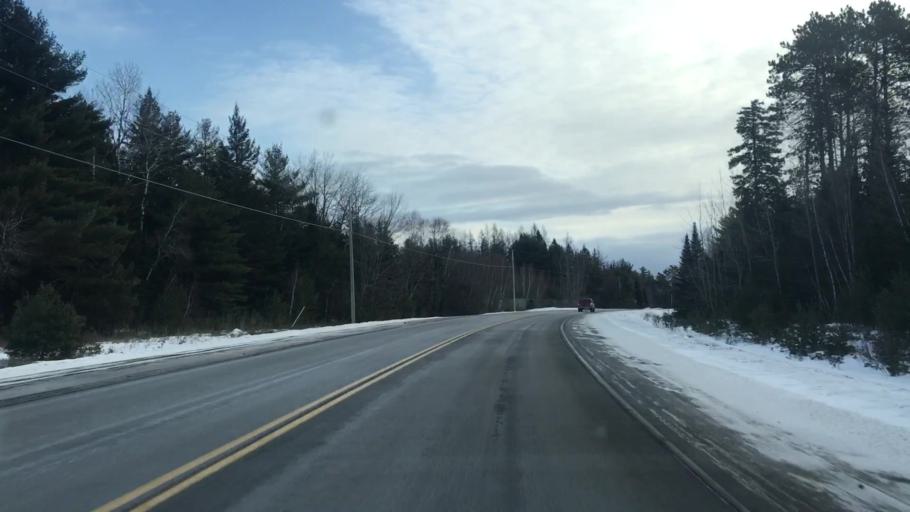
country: US
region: Maine
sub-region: Washington County
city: Addison
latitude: 44.9403
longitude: -67.7272
